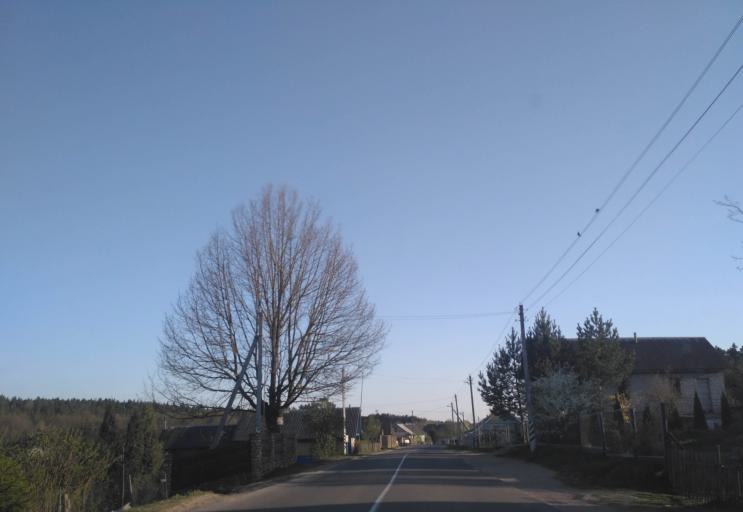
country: BY
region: Minsk
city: Radashkovichy
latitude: 54.1512
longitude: 27.2173
